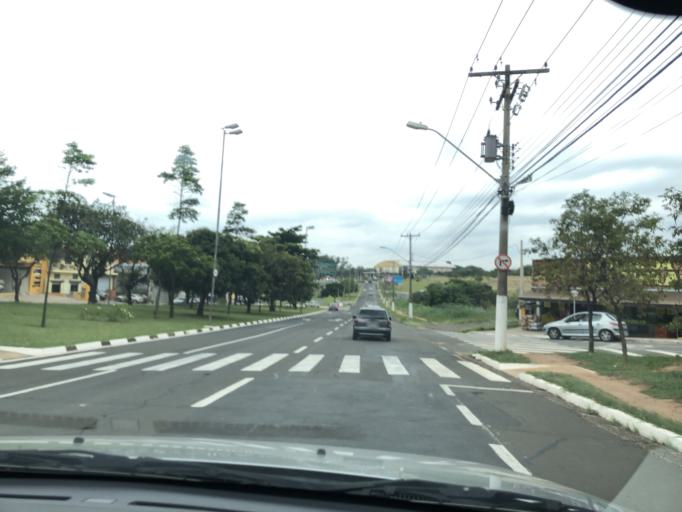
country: BR
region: Sao Paulo
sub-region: Paulinia
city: Paulinia
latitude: -22.7410
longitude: -47.1739
